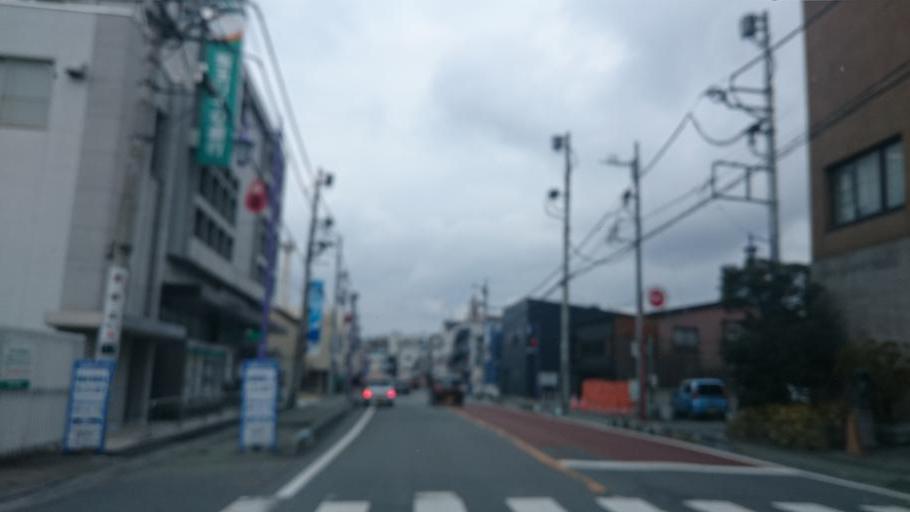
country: JP
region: Saitama
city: Chichibu
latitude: 35.9951
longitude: 139.0816
